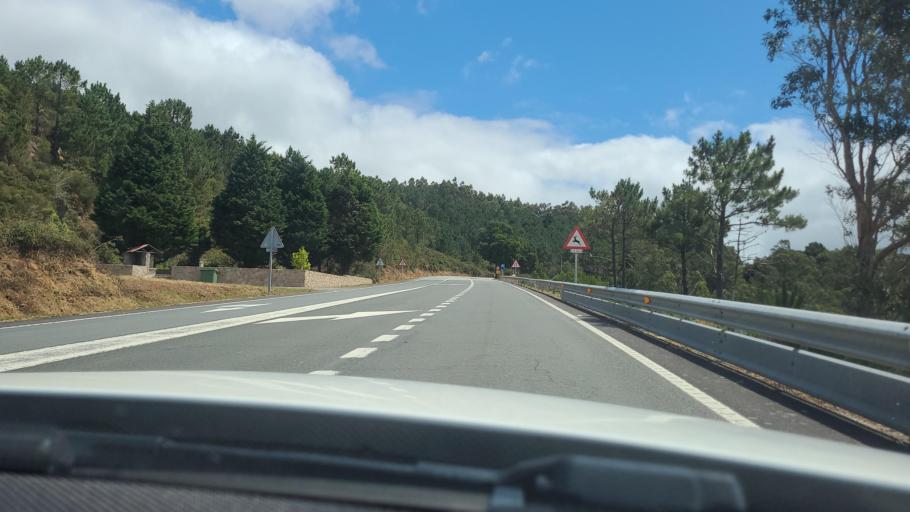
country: ES
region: Galicia
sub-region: Provincia da Coruna
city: Corcubion
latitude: 42.9234
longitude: -9.1587
